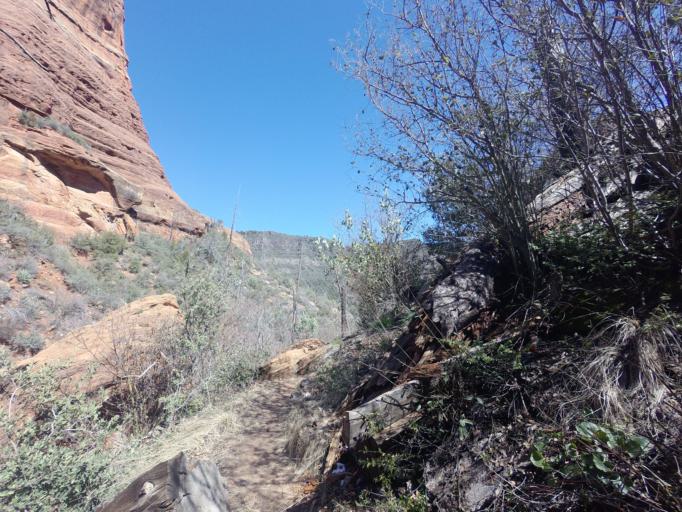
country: US
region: Arizona
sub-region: Coconino County
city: Sedona
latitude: 34.9348
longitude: -111.7522
